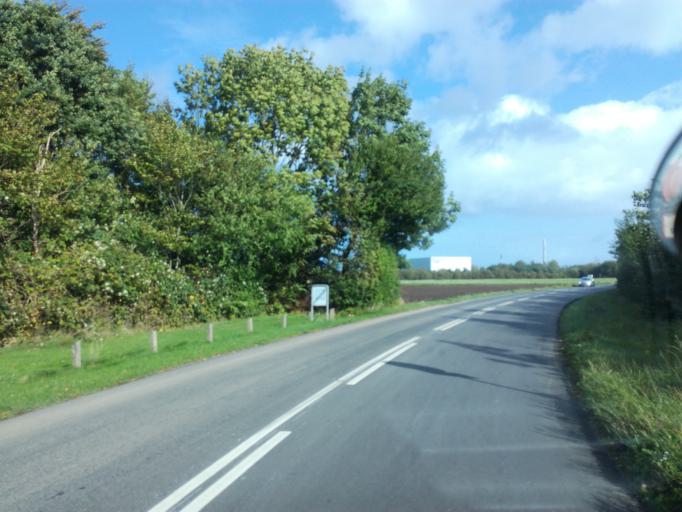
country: DK
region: South Denmark
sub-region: Fredericia Kommune
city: Fredericia
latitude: 55.5822
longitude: 9.7059
